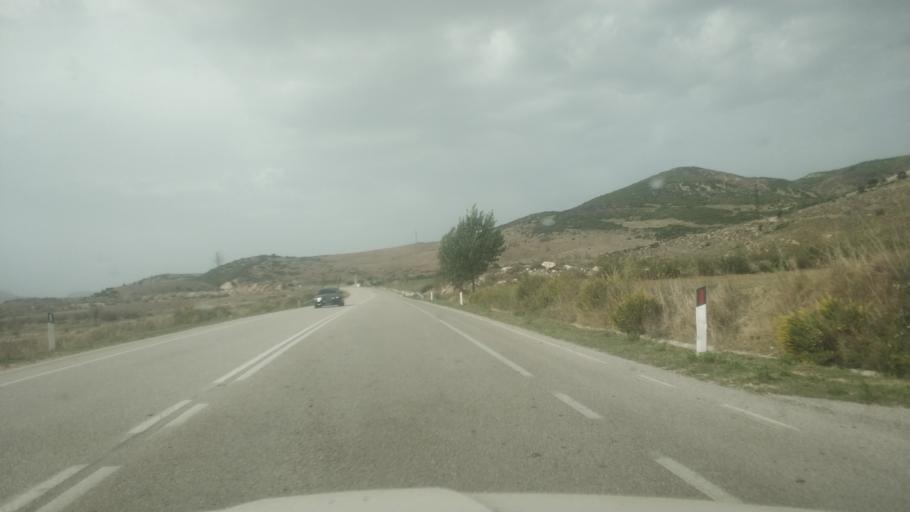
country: AL
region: Gjirokaster
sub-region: Rrethi i Tepelenes
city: Memaliaj
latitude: 40.3613
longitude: 19.9285
